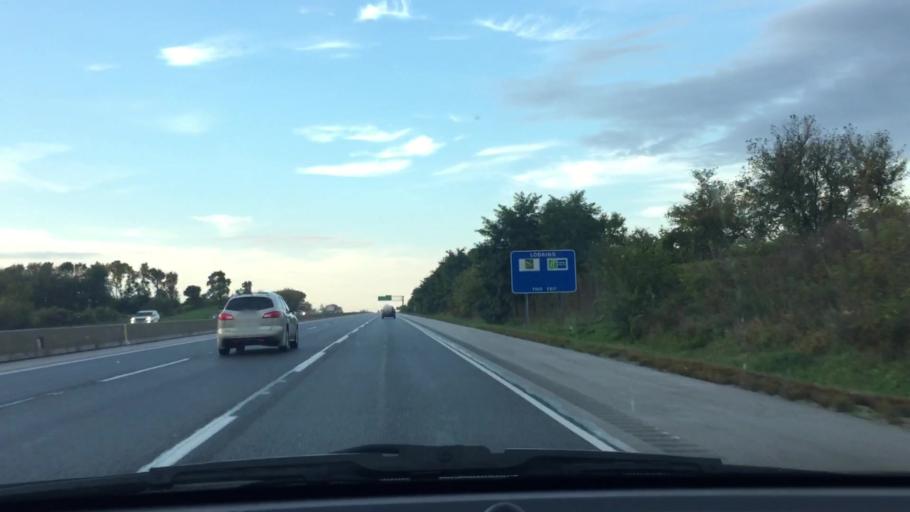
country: US
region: Illinois
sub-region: Winnebago County
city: Machesney Park
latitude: 42.3422
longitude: -88.9645
